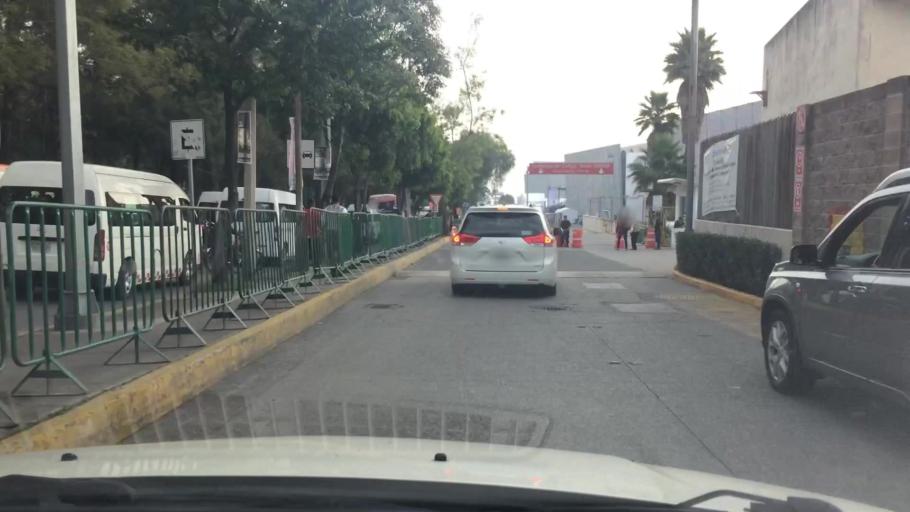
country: MX
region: Mexico City
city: Miguel Hidalgo
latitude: 19.4394
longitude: -99.2266
